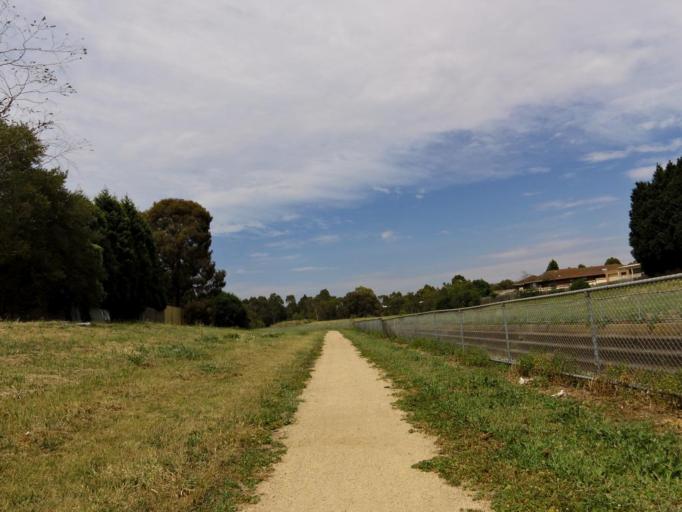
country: AU
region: Victoria
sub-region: Whittlesea
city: Epping
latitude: -37.6590
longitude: 145.0378
